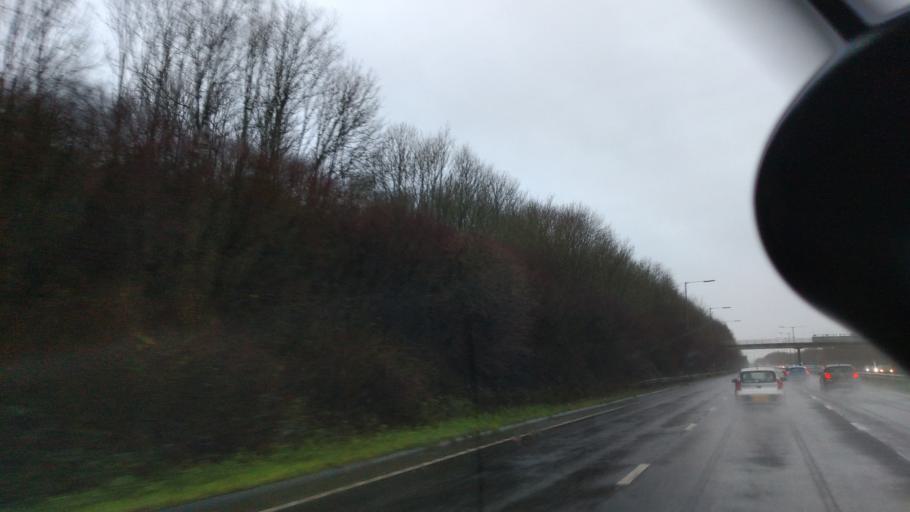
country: GB
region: England
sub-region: Brighton and Hove
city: Hove
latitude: 50.8644
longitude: -0.1656
